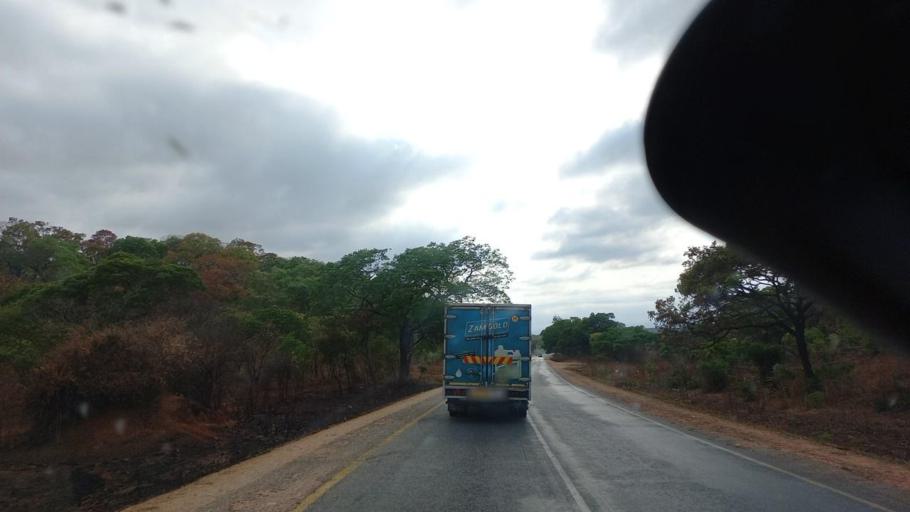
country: ZM
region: Lusaka
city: Chongwe
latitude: -15.2709
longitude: 28.8952
